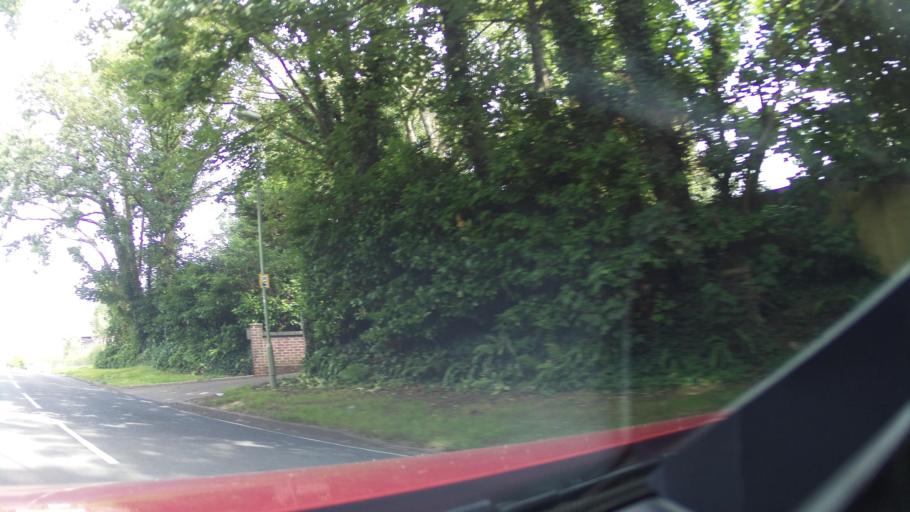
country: GB
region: England
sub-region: Hampshire
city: New Milton
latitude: 50.7516
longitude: -1.6798
